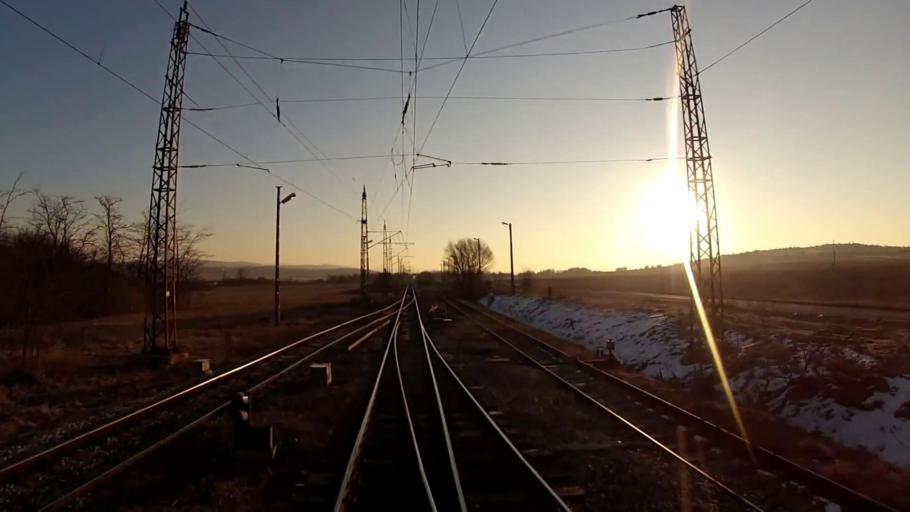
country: BG
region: Sofiya
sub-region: Obshtina Slivnitsa
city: Slivnitsa
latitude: 42.8803
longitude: 23.0146
